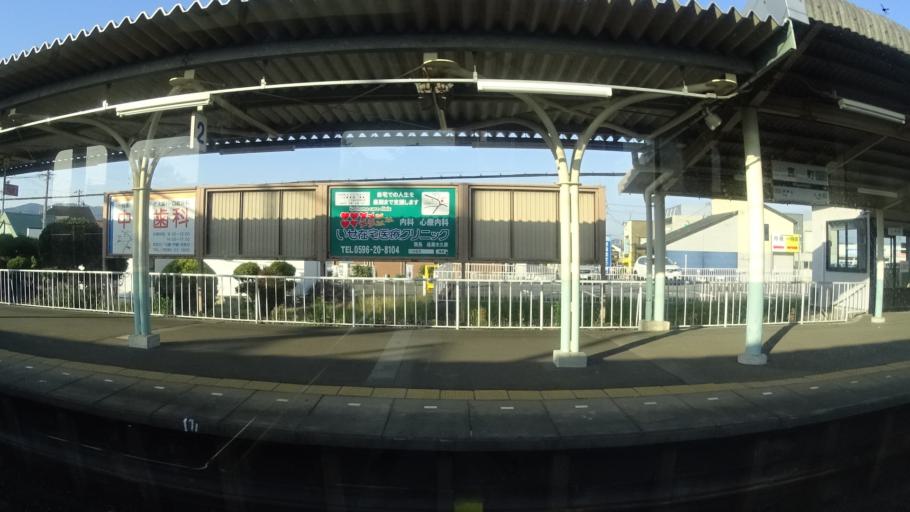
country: JP
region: Mie
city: Ise
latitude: 34.4976
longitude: 136.6987
